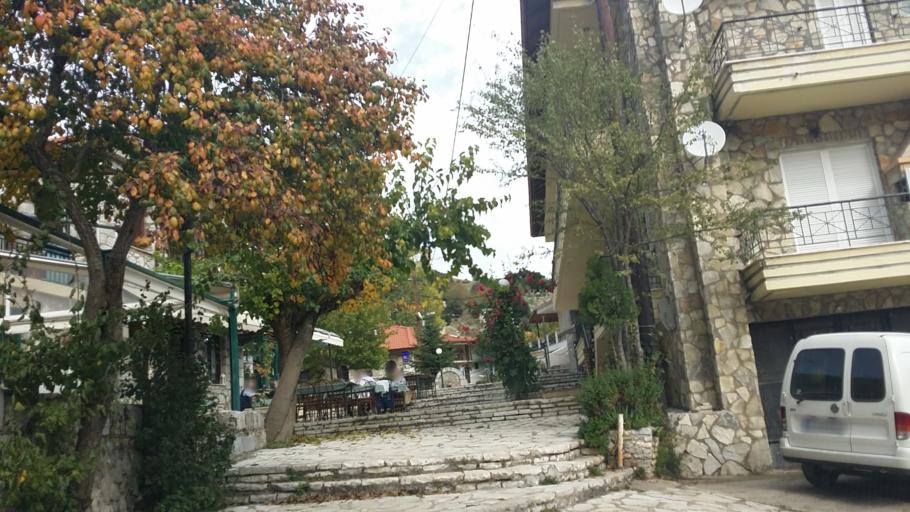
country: GR
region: Central Greece
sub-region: Nomos Voiotias
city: Kyriaki
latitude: 38.3652
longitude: 22.8396
